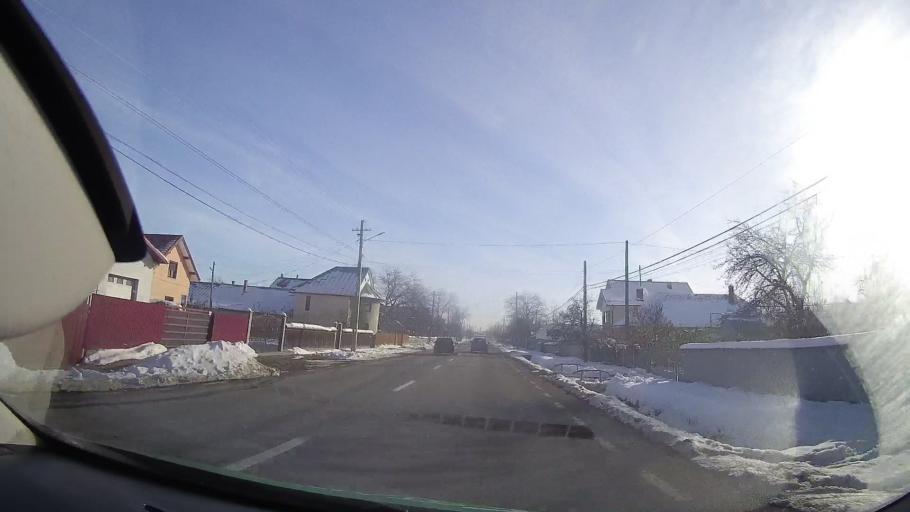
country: RO
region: Neamt
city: Bodesti
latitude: 47.0342
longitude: 26.4132
